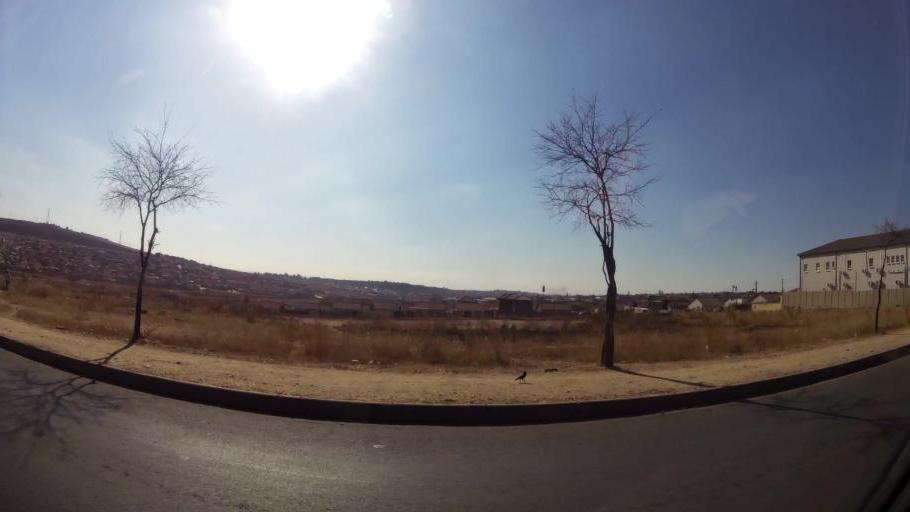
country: ZA
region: Gauteng
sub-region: West Rand District Municipality
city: Muldersdriseloop
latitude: -26.0366
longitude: 27.9216
